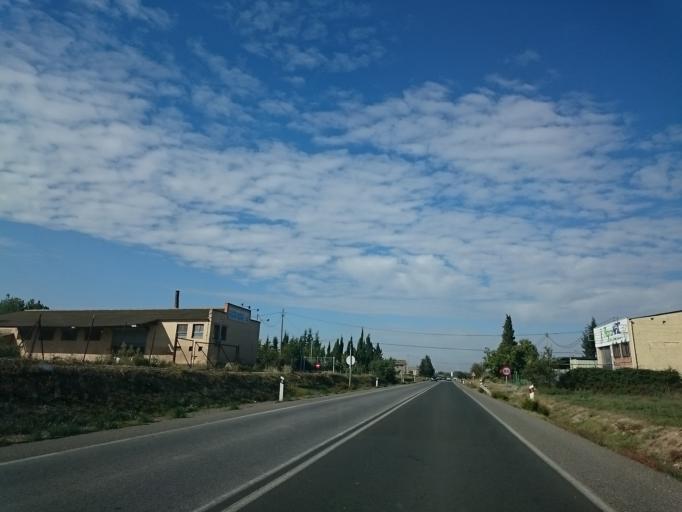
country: ES
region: Catalonia
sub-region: Provincia de Lleida
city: Juneda
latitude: 41.5407
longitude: 0.8271
